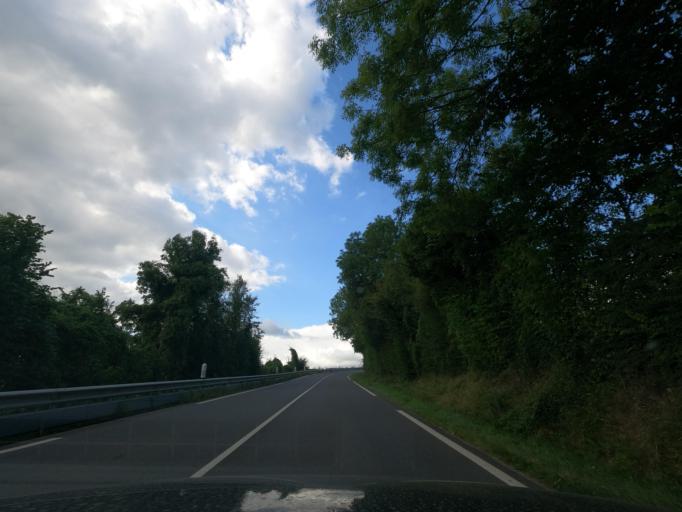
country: FR
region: Lower Normandy
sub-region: Departement de l'Orne
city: Gace
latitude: 48.8116
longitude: 0.3065
